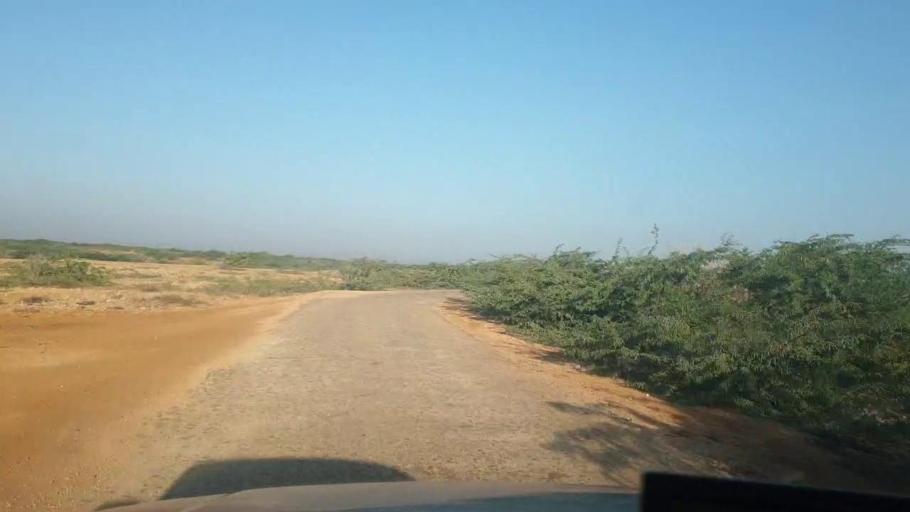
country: PK
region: Sindh
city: Thatta
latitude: 24.7069
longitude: 67.8479
